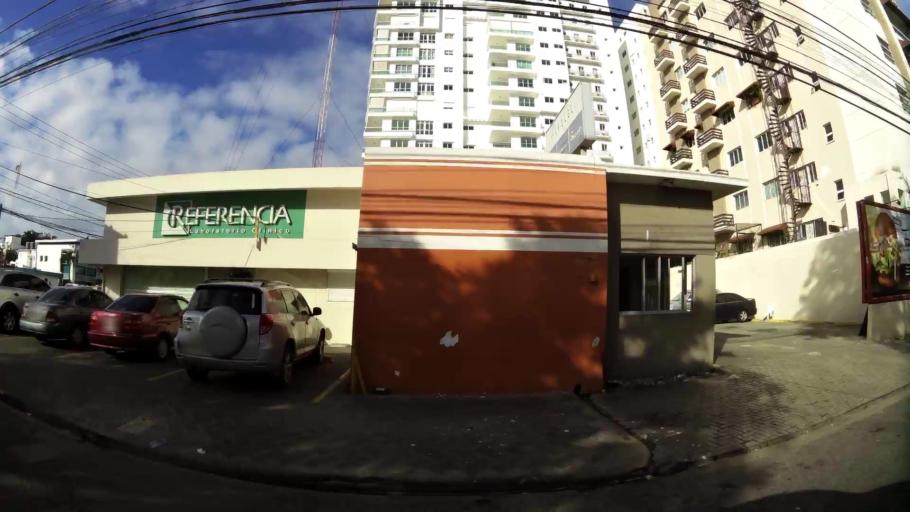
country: DO
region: Nacional
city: La Julia
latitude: 18.4684
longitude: -69.9344
